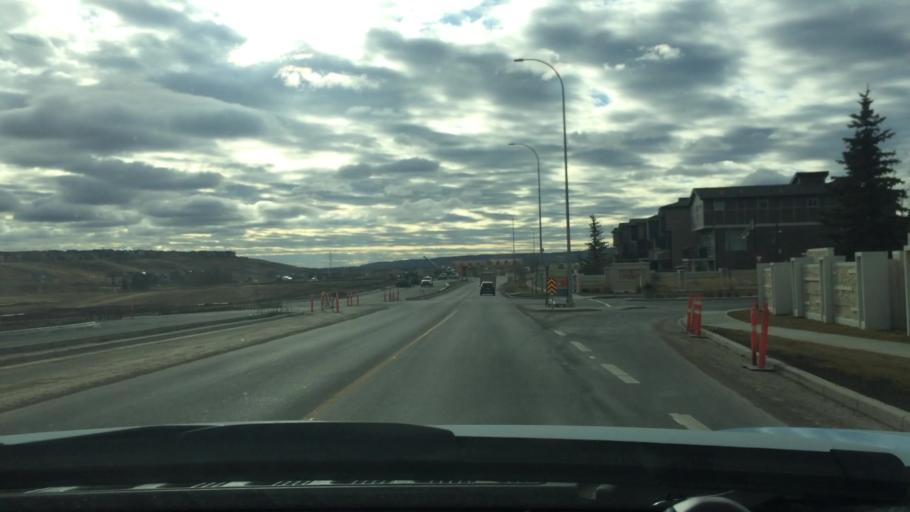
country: CA
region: Alberta
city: Calgary
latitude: 51.1812
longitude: -114.1343
